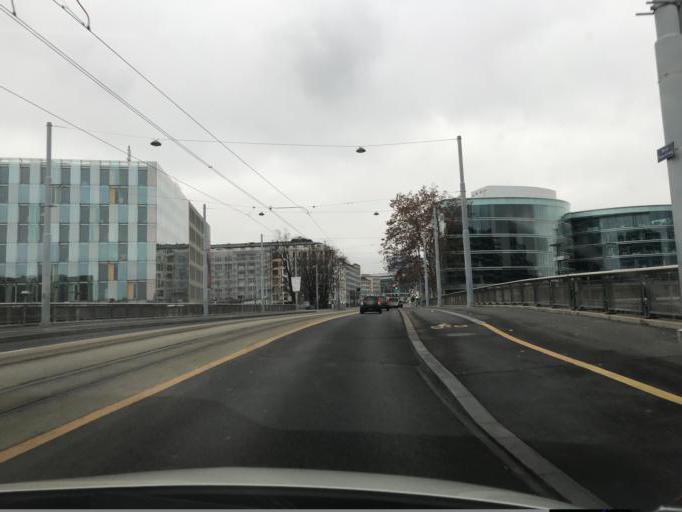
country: CH
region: Geneva
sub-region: Geneva
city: Geneve
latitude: 46.2201
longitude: 6.1453
